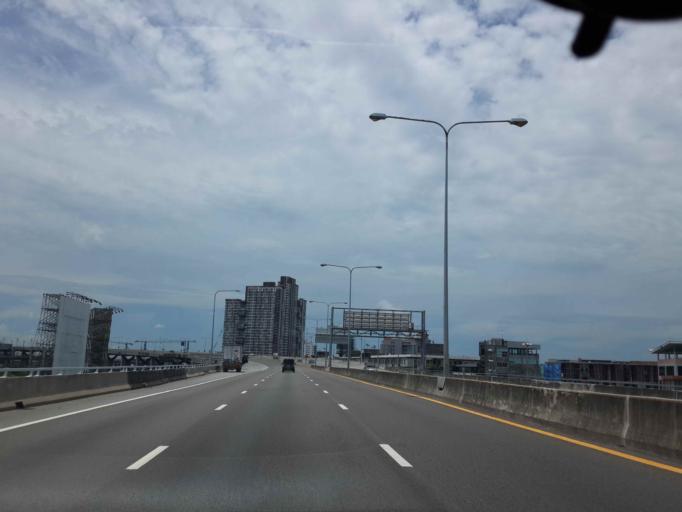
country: TH
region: Bangkok
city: Phra Khanong
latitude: 13.6785
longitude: 100.6038
